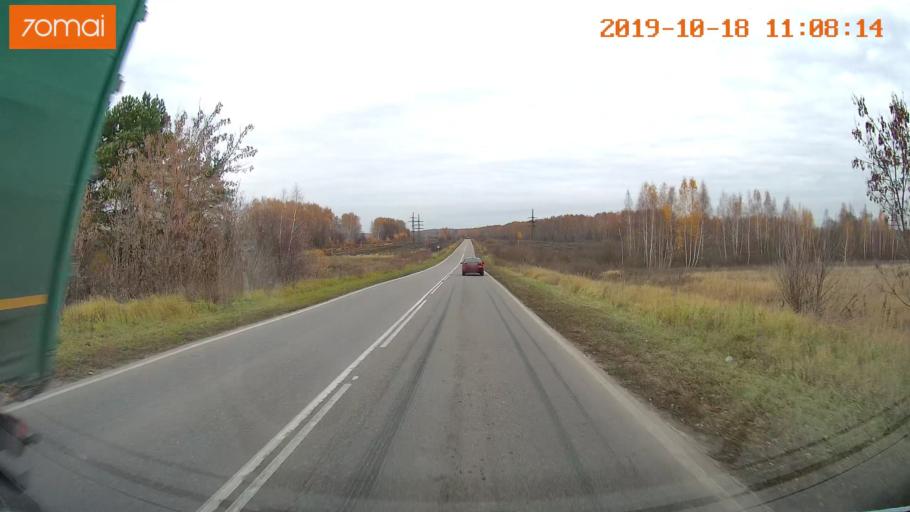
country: RU
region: Tula
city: Kimovsk
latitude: 53.9348
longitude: 38.5383
